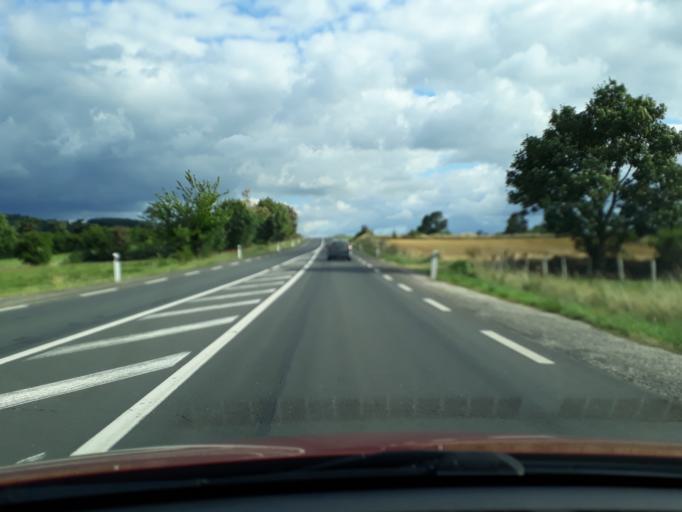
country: FR
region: Auvergne
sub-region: Departement de la Haute-Loire
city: Solignac-sur-Loire
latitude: 44.9099
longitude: 3.8493
